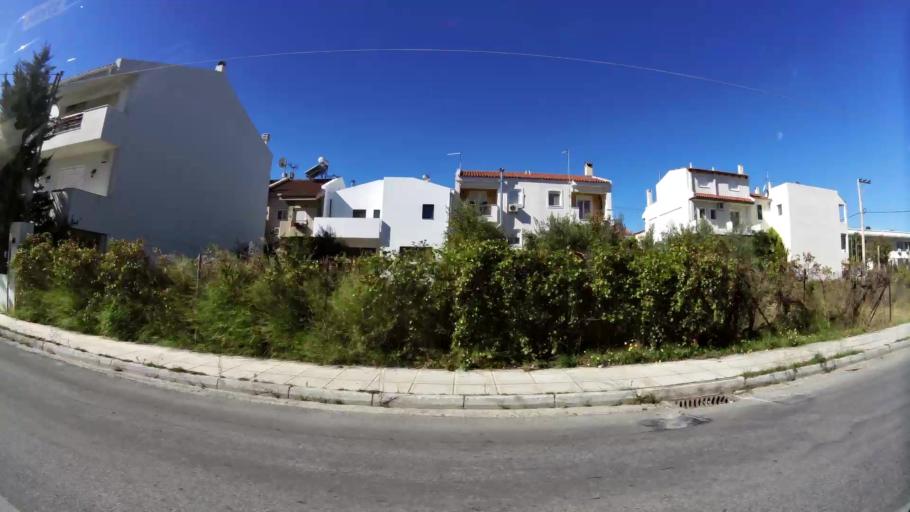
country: GR
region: Attica
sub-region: Nomarchia Anatolikis Attikis
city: Leondarion
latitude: 38.0037
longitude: 23.8578
